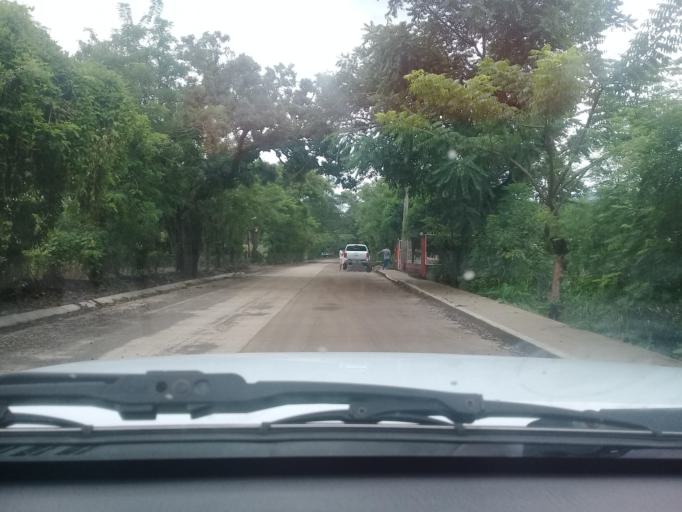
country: MX
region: Veracruz
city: Comoapan
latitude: 18.4121
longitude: -95.1802
